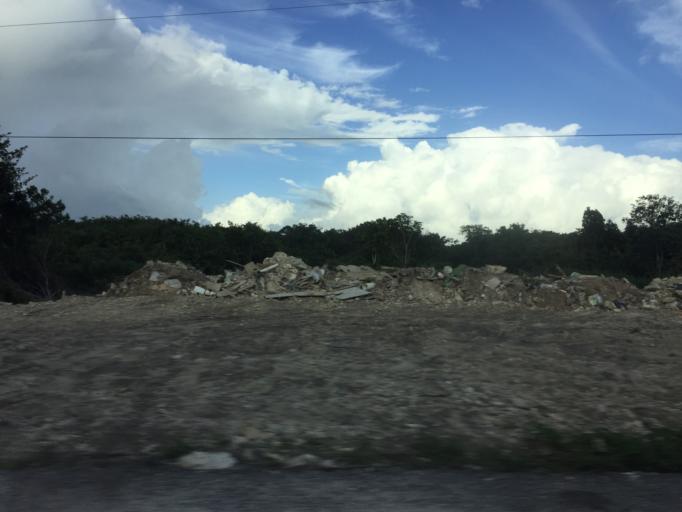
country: MX
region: Quintana Roo
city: Tulum
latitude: 20.2603
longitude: -87.4717
